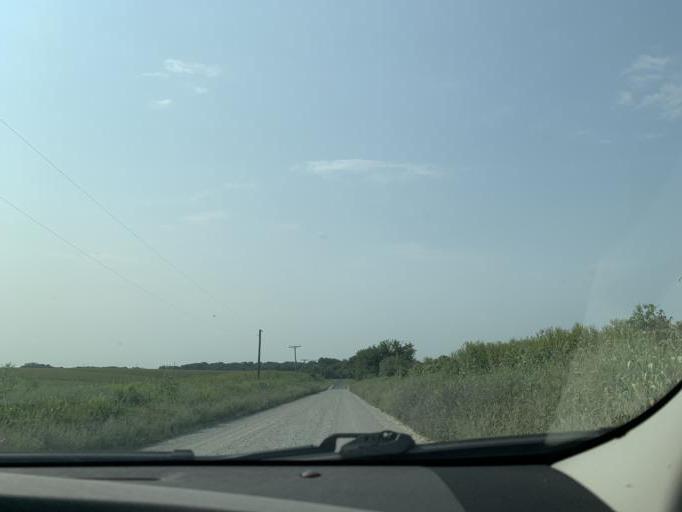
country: US
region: Illinois
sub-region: Whiteside County
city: Sterling
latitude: 41.8269
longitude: -89.7471
